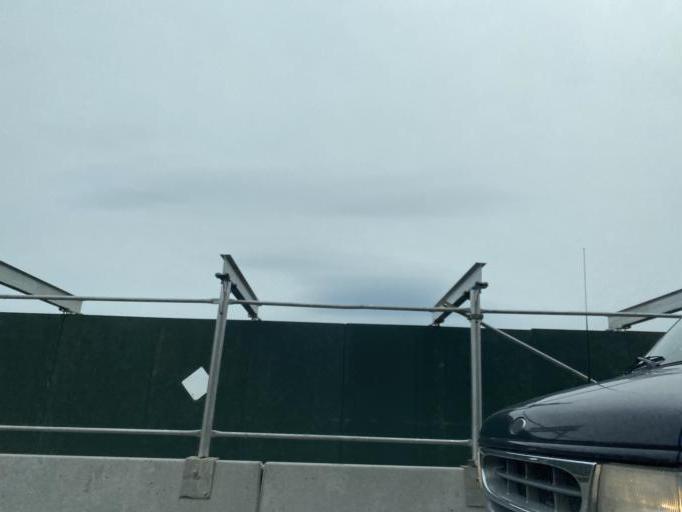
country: US
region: New York
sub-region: Queens County
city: Jamaica
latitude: 40.6663
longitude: -73.8099
